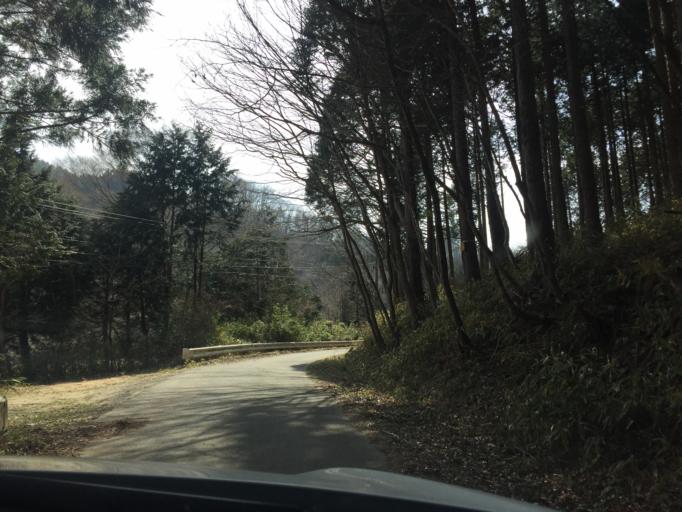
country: JP
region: Fukushima
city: Iwaki
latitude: 37.1274
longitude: 140.7809
